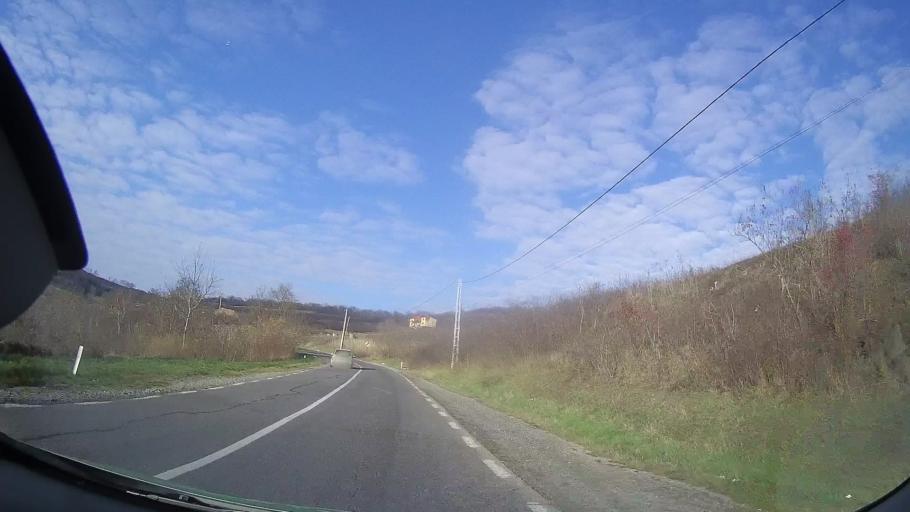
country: RO
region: Cluj
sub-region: Comuna Cojocna
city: Cojocna
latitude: 46.8075
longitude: 23.8405
